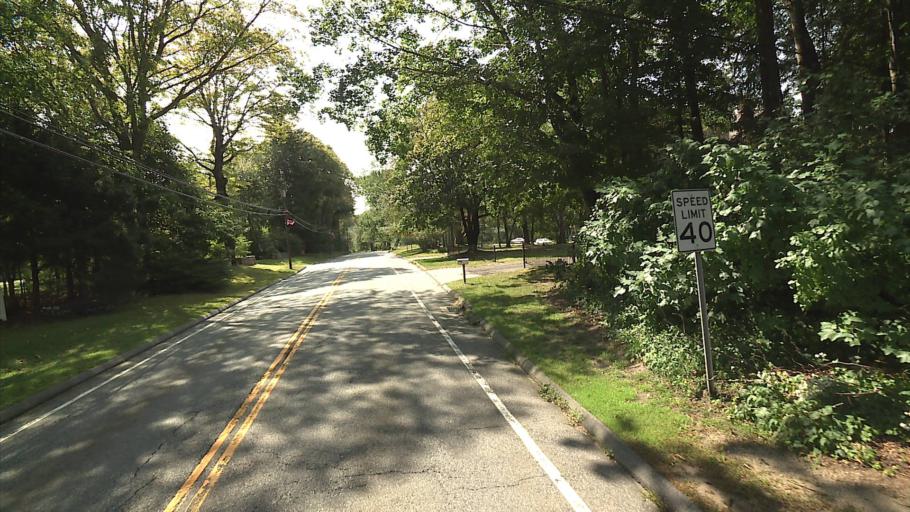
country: US
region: Connecticut
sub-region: Windham County
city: South Woodstock
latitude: 41.8806
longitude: -71.9618
